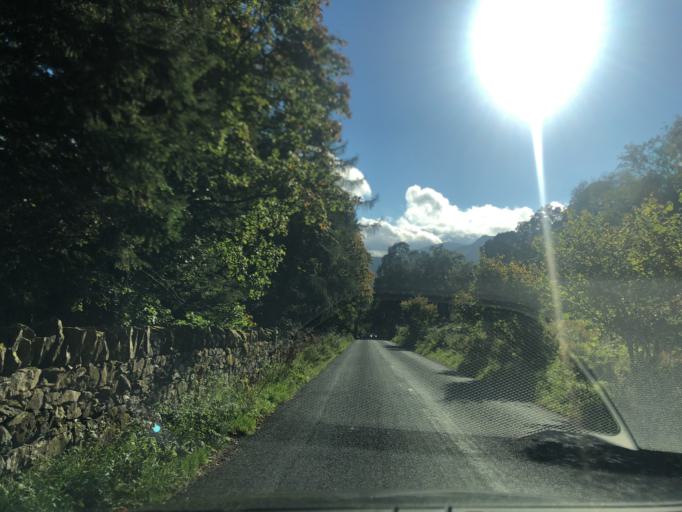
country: GB
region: England
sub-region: Cumbria
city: Ambleside
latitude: 54.5774
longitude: -2.9326
